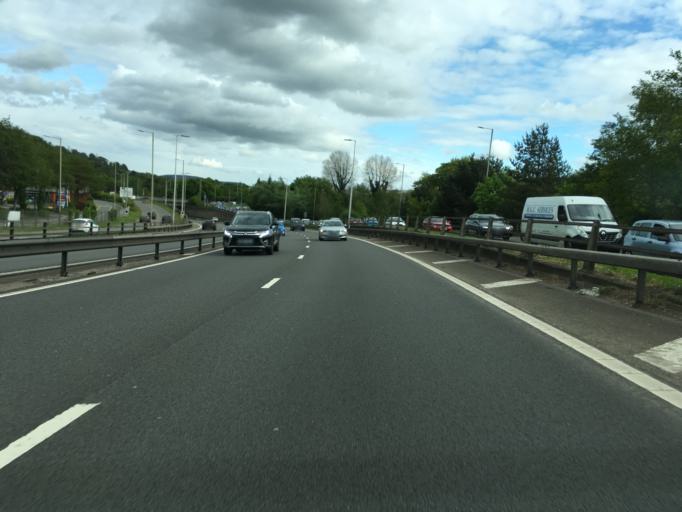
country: GB
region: Wales
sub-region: Rhondda Cynon Taf
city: Pontypridd
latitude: 51.6024
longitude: -3.3351
